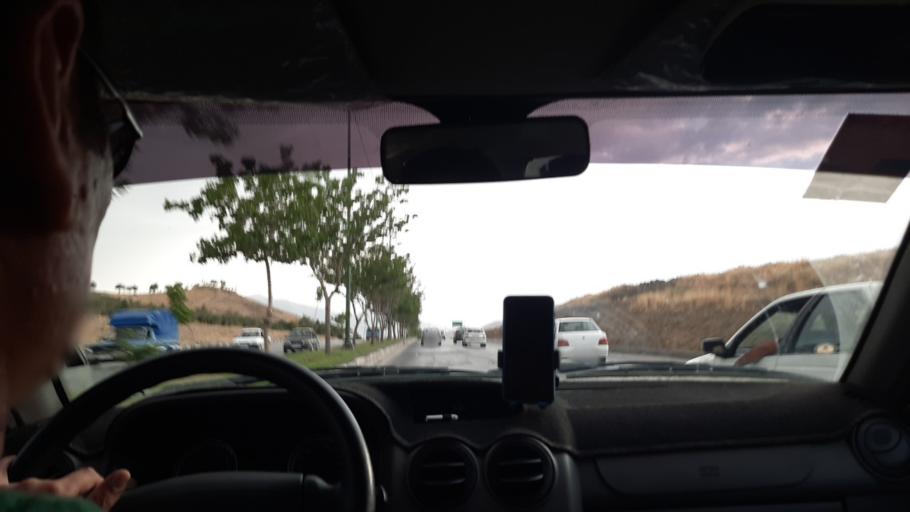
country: IR
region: Markazi
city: Arak
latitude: 34.0809
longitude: 49.6533
